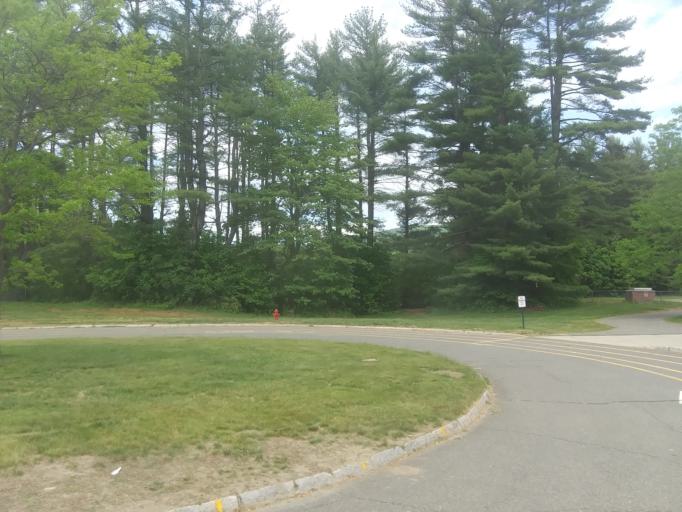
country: US
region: Massachusetts
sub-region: Franklin County
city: Shelburne Falls
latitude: 42.6158
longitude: -72.7568
